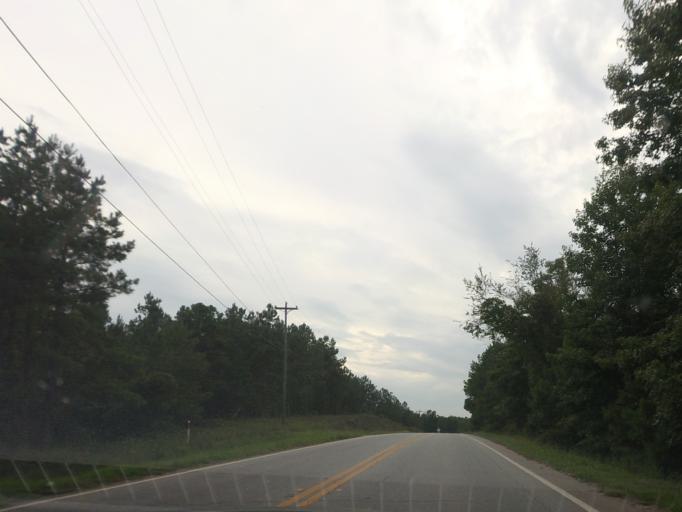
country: US
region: Georgia
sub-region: Twiggs County
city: Jeffersonville
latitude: 32.7655
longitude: -83.4749
